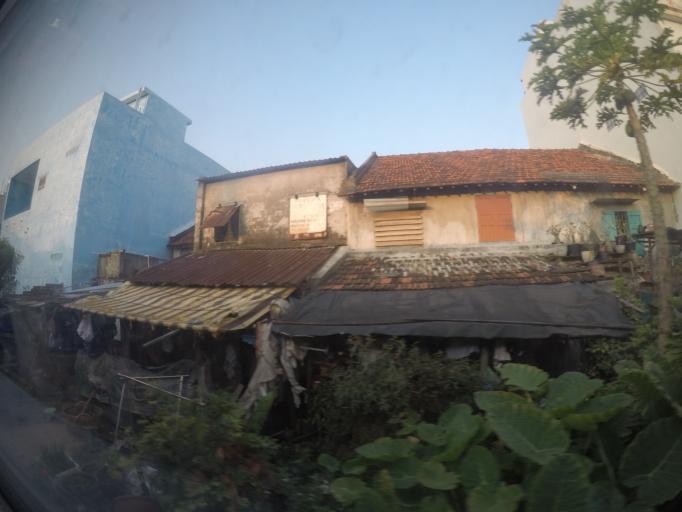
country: VN
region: Phu Yen
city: Tuy Hoa
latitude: 13.0926
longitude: 109.2948
